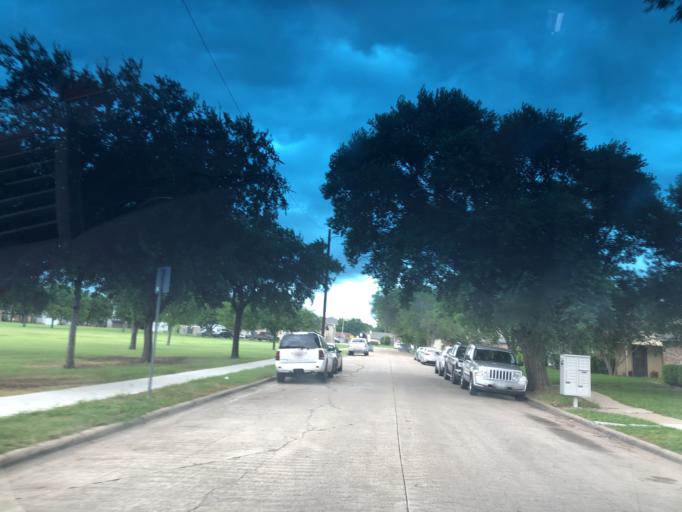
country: US
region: Texas
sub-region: Dallas County
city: Grand Prairie
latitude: 32.7000
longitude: -97.0096
